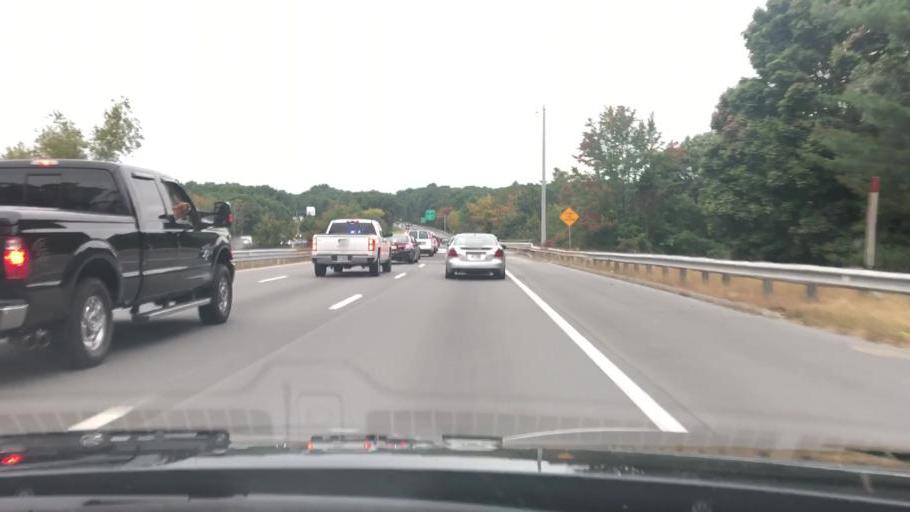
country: US
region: Massachusetts
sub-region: Essex County
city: Lawrence
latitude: 42.6753
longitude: -71.1711
